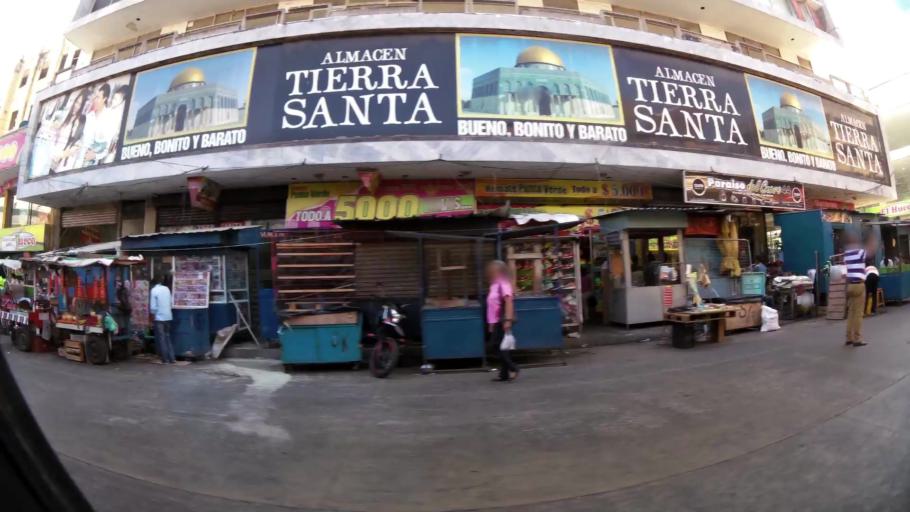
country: CO
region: Atlantico
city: Barranquilla
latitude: 10.9832
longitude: -74.7793
